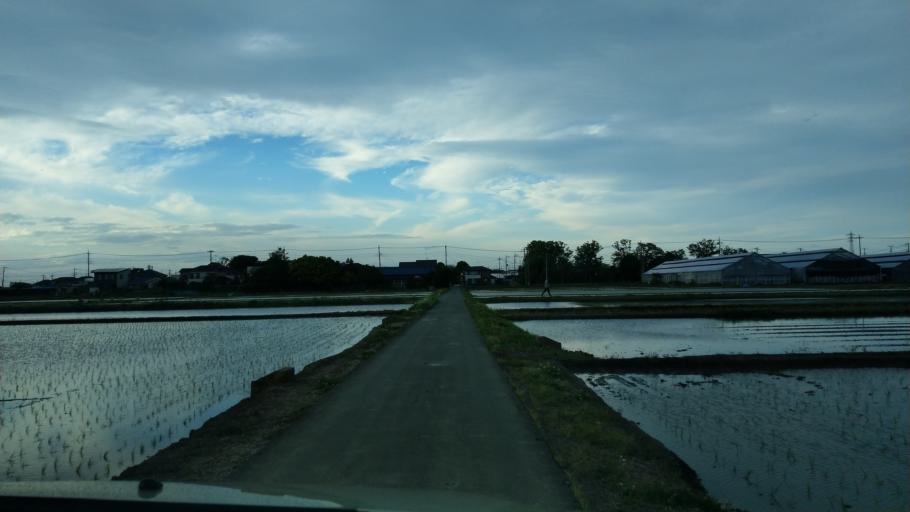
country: JP
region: Saitama
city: Yono
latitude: 35.8806
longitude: 139.5929
